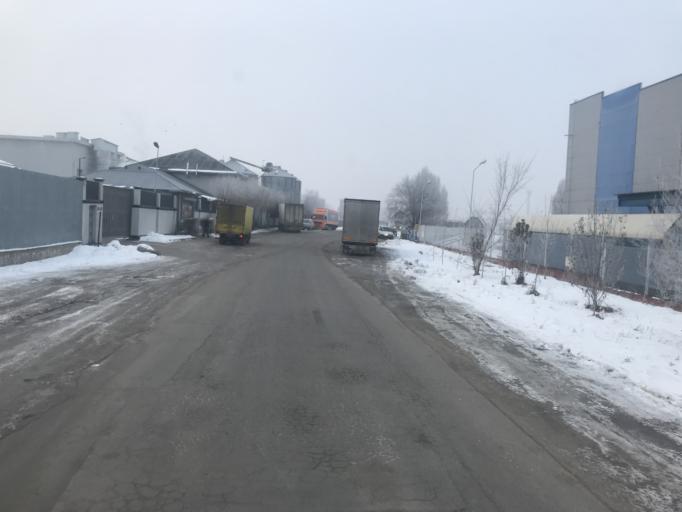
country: KZ
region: Almaty Oblysy
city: Pervomayskiy
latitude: 43.3614
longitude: 76.9778
